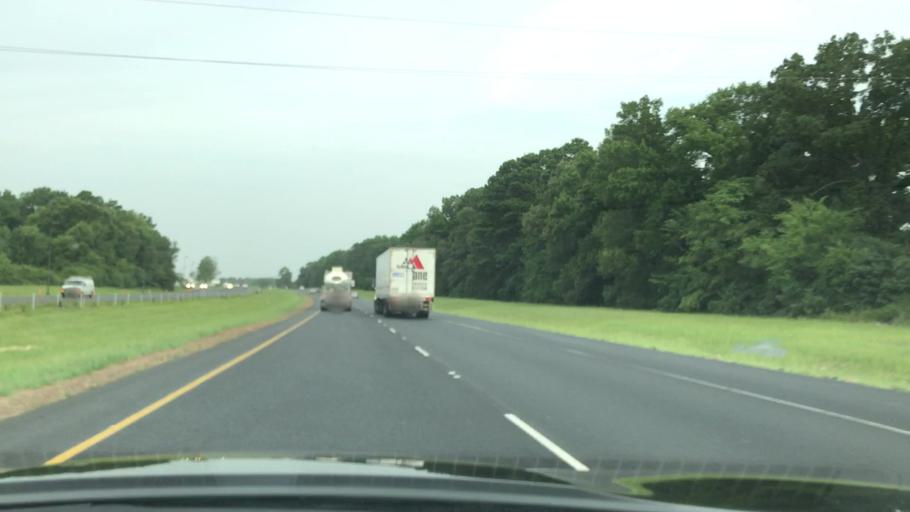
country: US
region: Louisiana
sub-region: Caddo Parish
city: Greenwood
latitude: 32.4509
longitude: -93.9941
